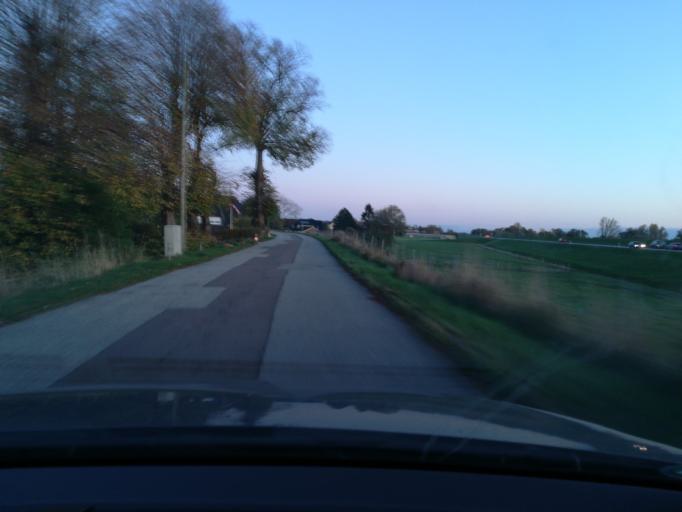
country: DE
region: Lower Saxony
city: Stelle
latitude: 53.4107
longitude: 10.1542
